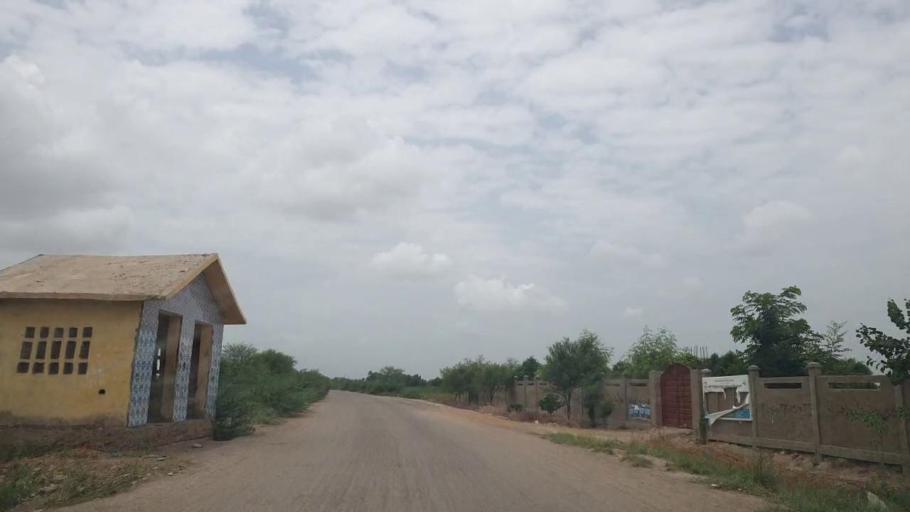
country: PK
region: Sindh
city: Naukot
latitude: 24.9144
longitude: 69.2707
